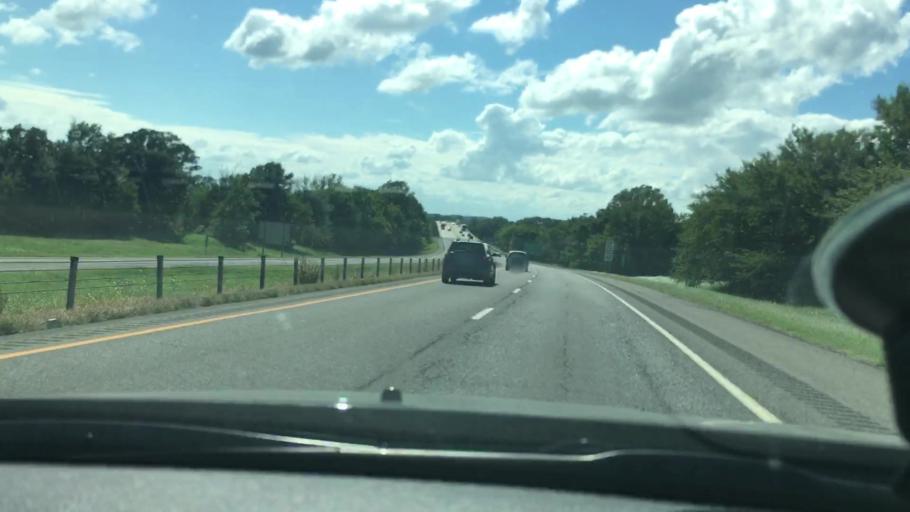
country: US
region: Oklahoma
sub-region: Sequoyah County
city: Vian
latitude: 35.4897
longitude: -95.0888
